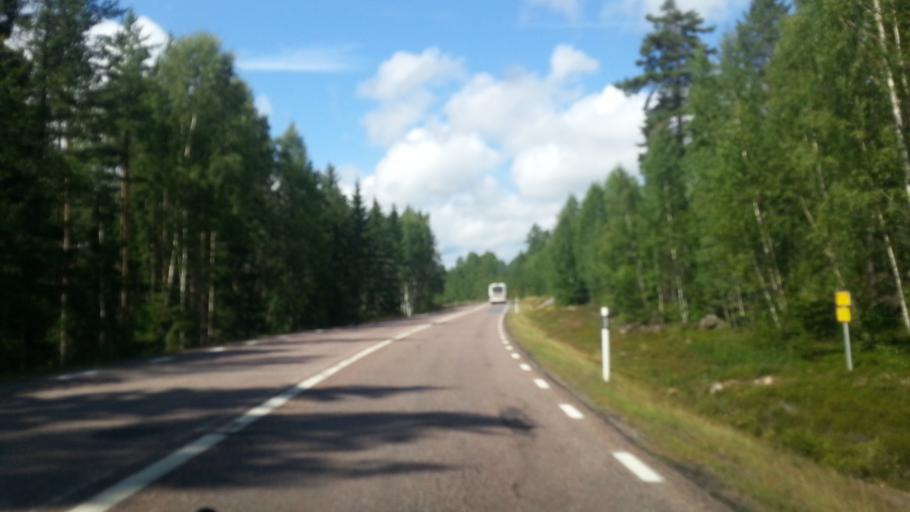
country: SE
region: Dalarna
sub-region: Faluns Kommun
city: Falun
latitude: 60.6126
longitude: 15.7320
